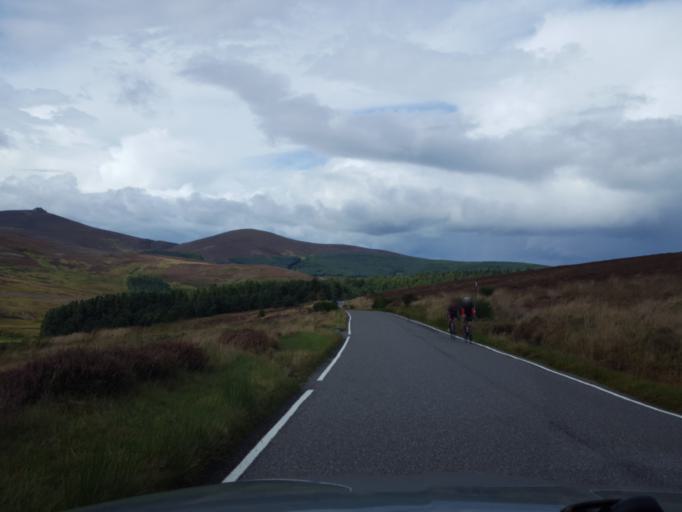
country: GB
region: Scotland
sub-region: Aberdeenshire
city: Banchory
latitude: 56.9432
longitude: -2.5761
